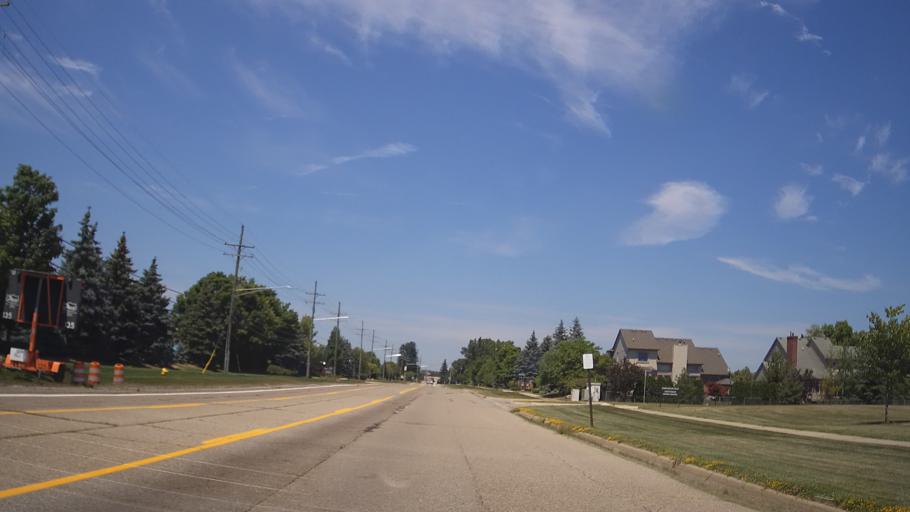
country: US
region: Michigan
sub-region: Macomb County
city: Clinton
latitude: 42.6479
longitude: -82.9167
